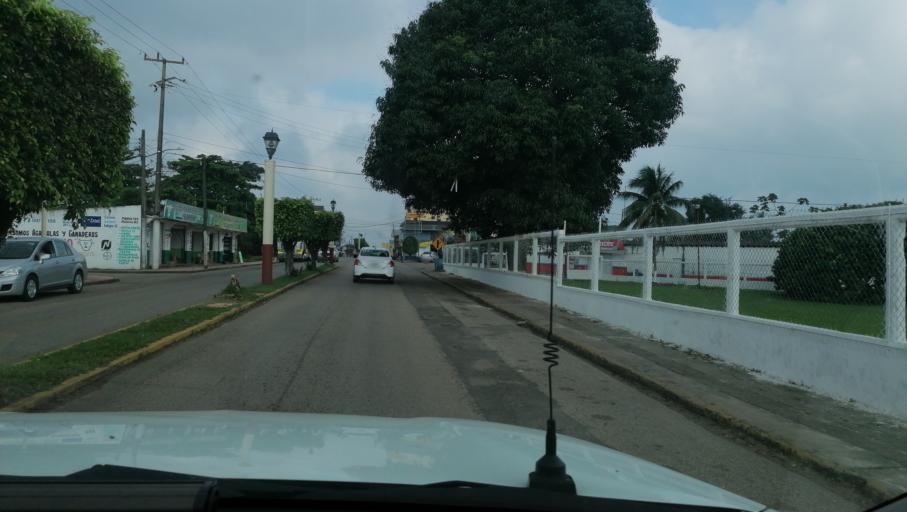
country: MX
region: Chiapas
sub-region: Juarez
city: El Triunfo 1ra. Seccion (Cardona)
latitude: 17.6042
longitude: -93.1876
